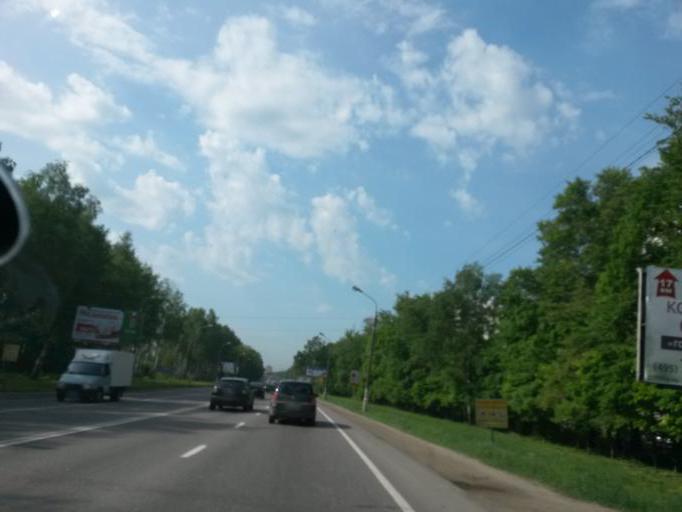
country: RU
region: Moskovskaya
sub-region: Chekhovskiy Rayon
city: Chekhov
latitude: 55.1711
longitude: 37.4709
